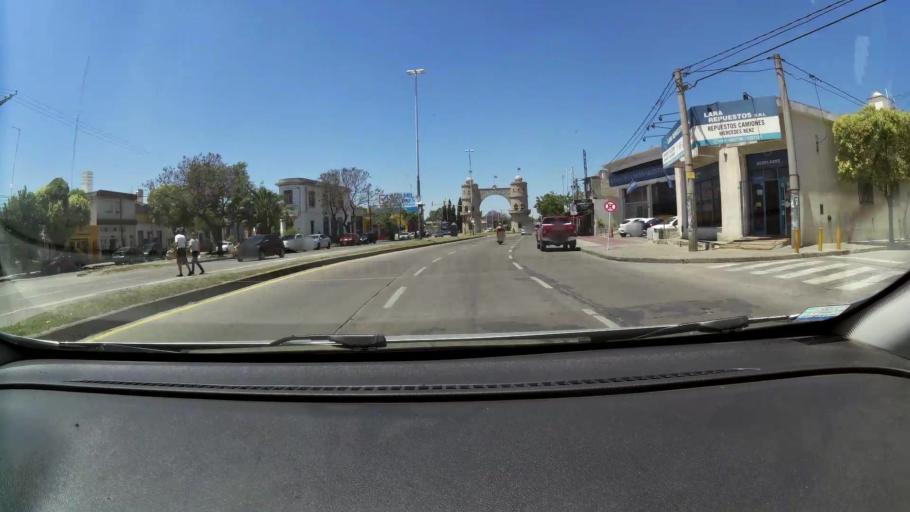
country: AR
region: Cordoba
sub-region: Departamento de Capital
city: Cordoba
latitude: -31.4371
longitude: -64.1293
